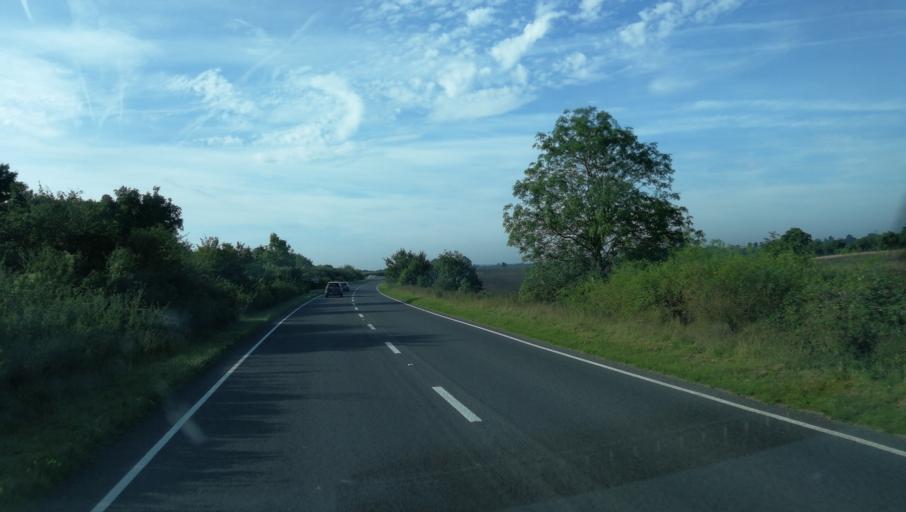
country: GB
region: England
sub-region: Oxfordshire
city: Woodstock
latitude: 51.8935
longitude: -1.3269
